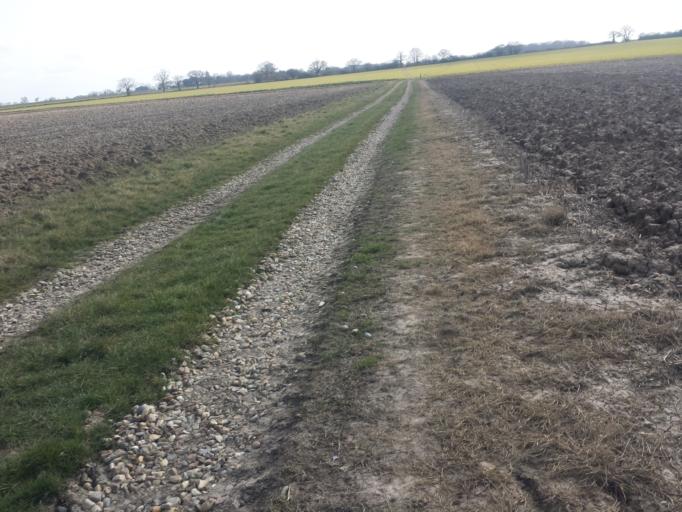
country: GB
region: England
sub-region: Essex
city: Mistley
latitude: 51.9067
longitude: 1.1520
